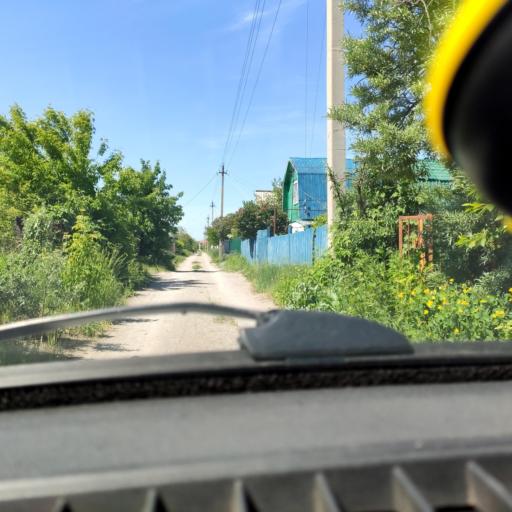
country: RU
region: Samara
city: Povolzhskiy
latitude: 53.6148
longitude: 49.6209
